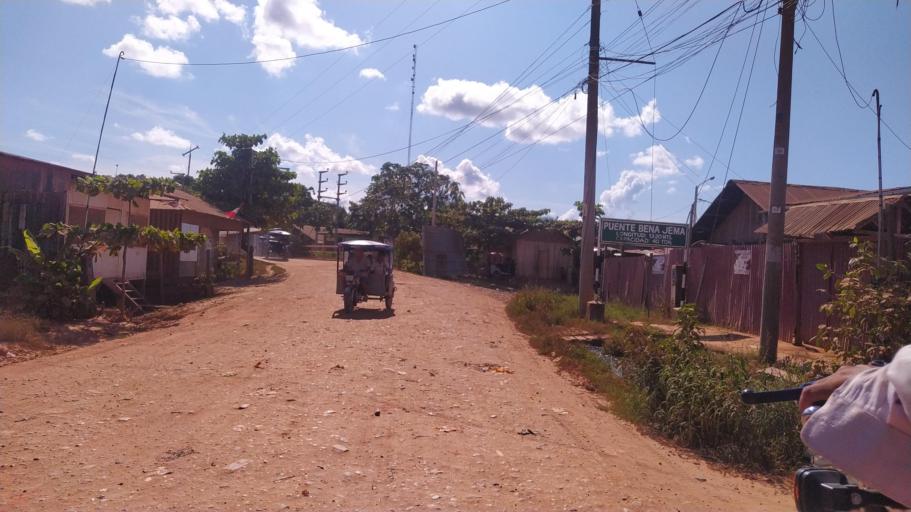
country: PE
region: Ucayali
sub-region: Provincia de Coronel Portillo
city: Puerto Callao
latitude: -8.3592
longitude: -74.5844
